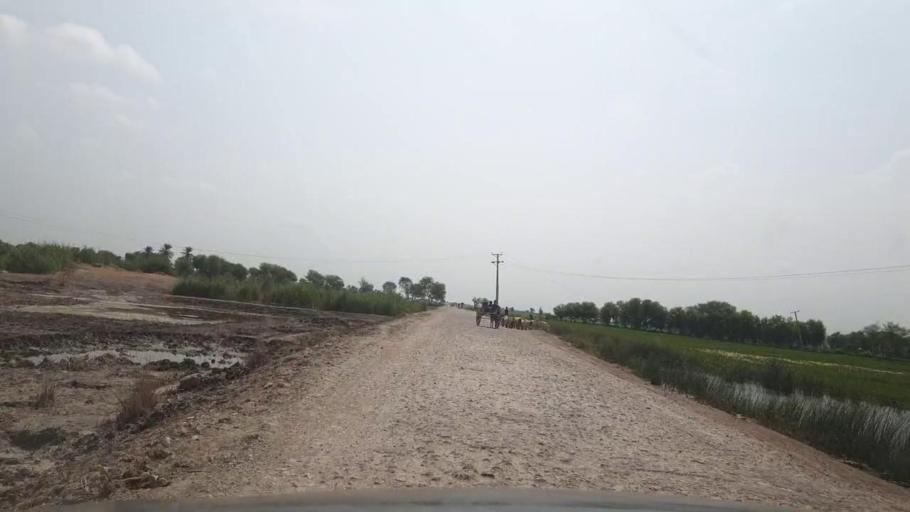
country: PK
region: Sindh
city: Ratodero
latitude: 27.8411
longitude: 68.3233
